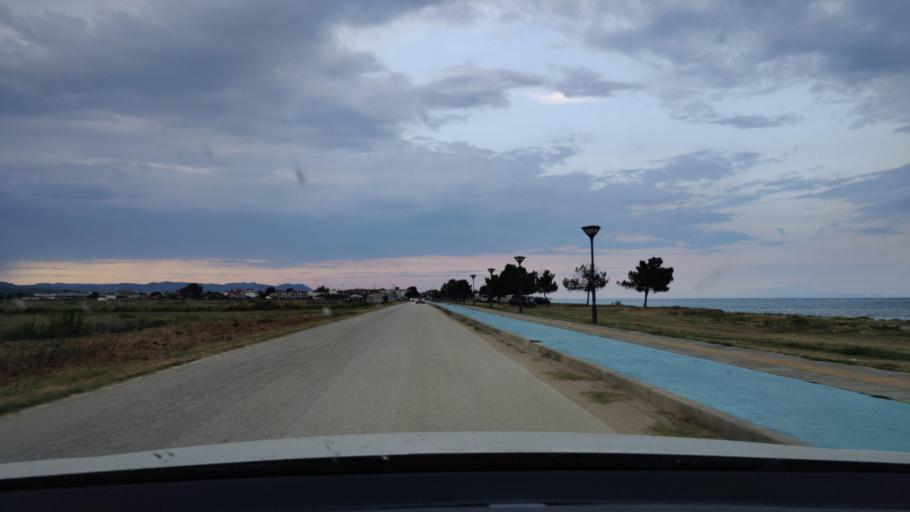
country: GR
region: East Macedonia and Thrace
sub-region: Nomos Kavalas
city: Paralia Ofryniou
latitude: 40.7689
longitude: 23.8923
